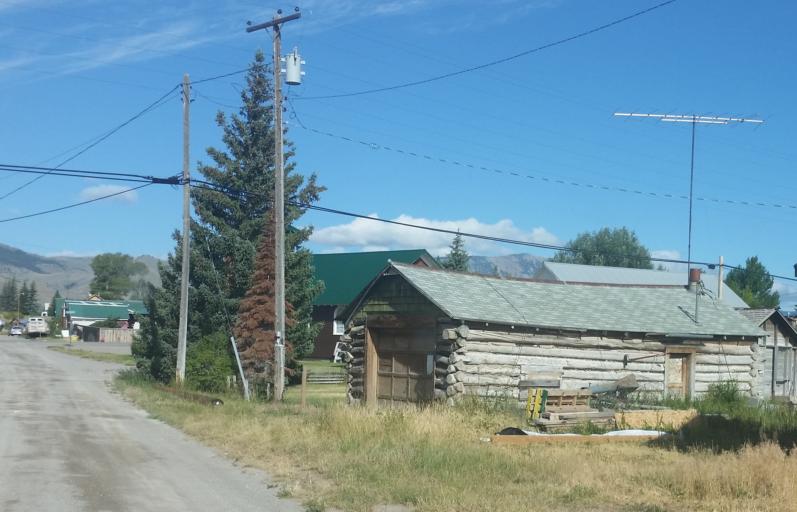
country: US
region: Montana
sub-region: Beaverhead County
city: Dillon
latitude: 44.6380
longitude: -112.5926
